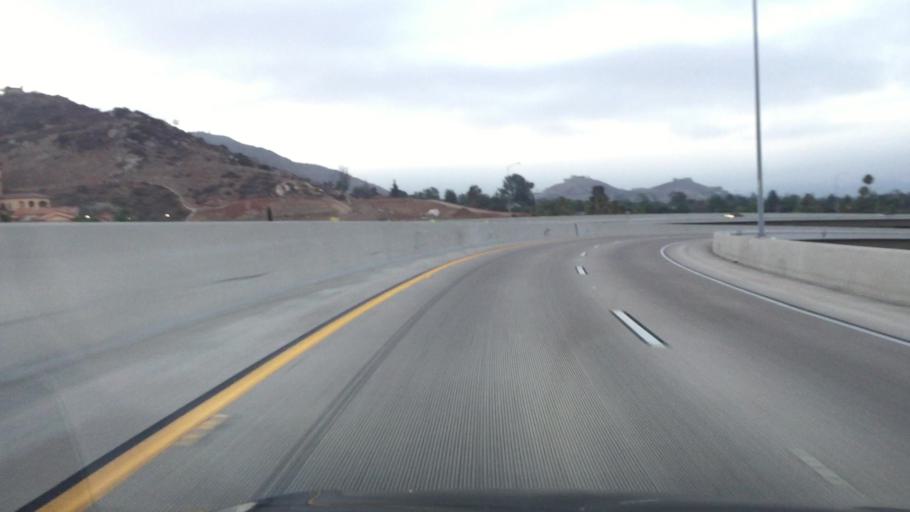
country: US
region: California
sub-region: San Diego County
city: Santee
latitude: 32.8319
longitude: -116.9636
